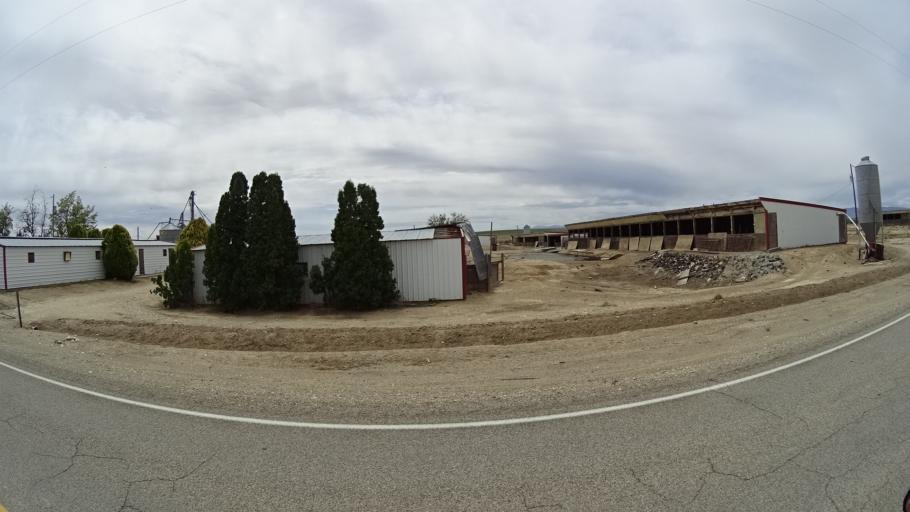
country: US
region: Idaho
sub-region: Ada County
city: Kuna
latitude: 43.4589
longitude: -116.4999
